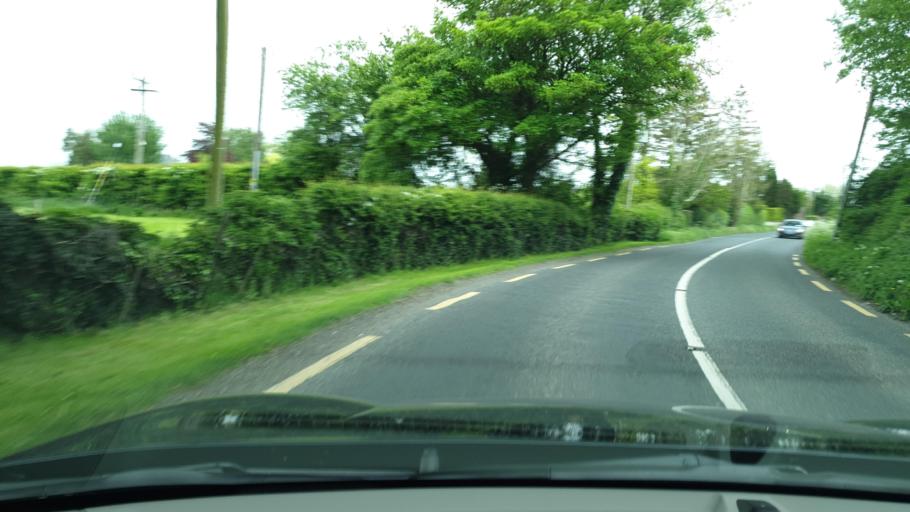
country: IE
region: Leinster
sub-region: An Mhi
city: Ratoath
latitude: 53.5070
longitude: -6.4433
